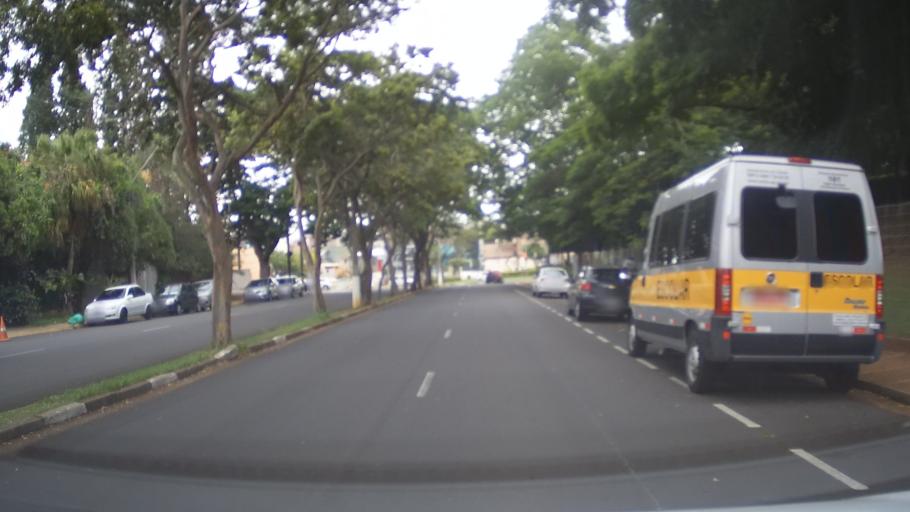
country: BR
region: Sao Paulo
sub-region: Campinas
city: Campinas
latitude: -22.9071
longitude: -47.0388
